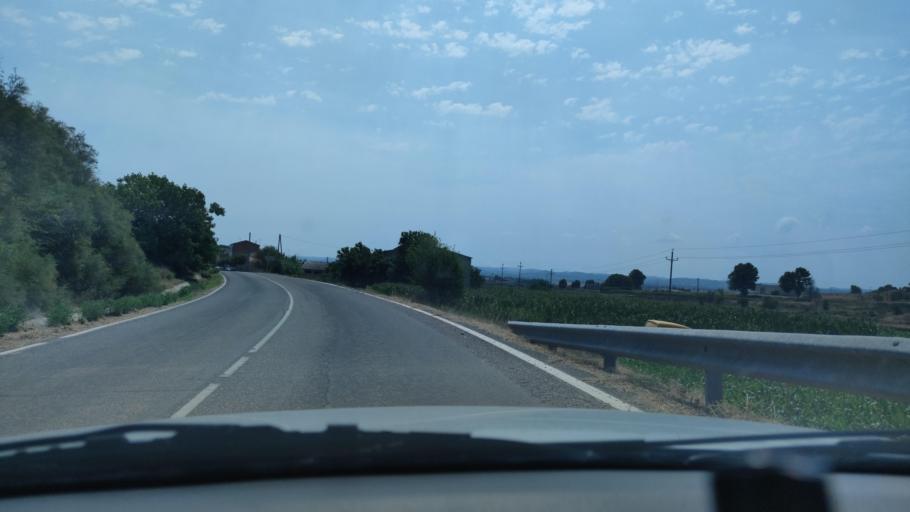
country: ES
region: Catalonia
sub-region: Provincia de Lleida
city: Bellpuig
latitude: 41.6087
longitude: 1.0319
